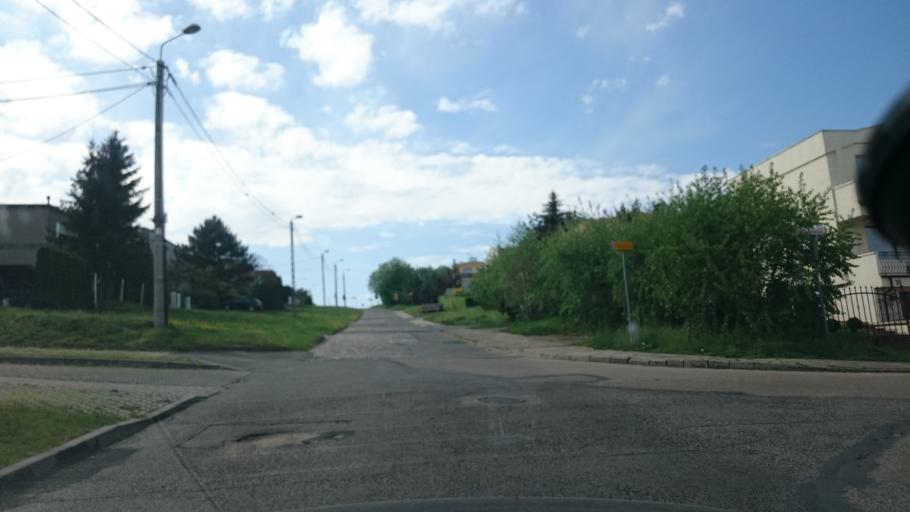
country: PL
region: Kujawsko-Pomorskie
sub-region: Grudziadz
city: Grudziadz
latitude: 53.4648
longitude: 18.7358
